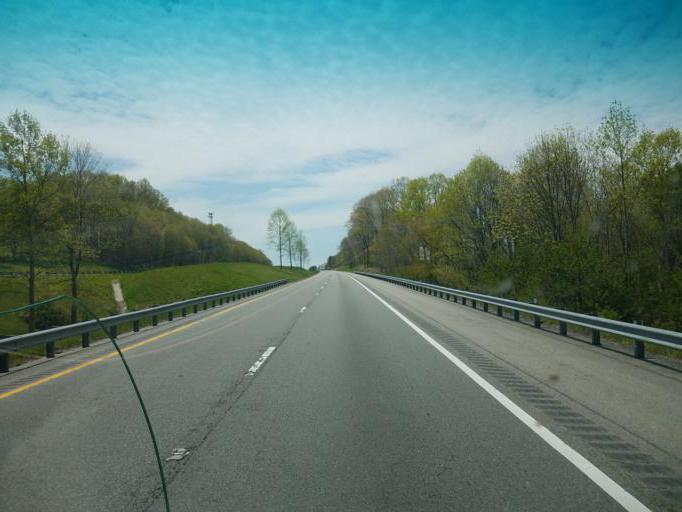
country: US
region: Virginia
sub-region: Wythe County
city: Rural Retreat
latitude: 36.9095
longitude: -81.3004
